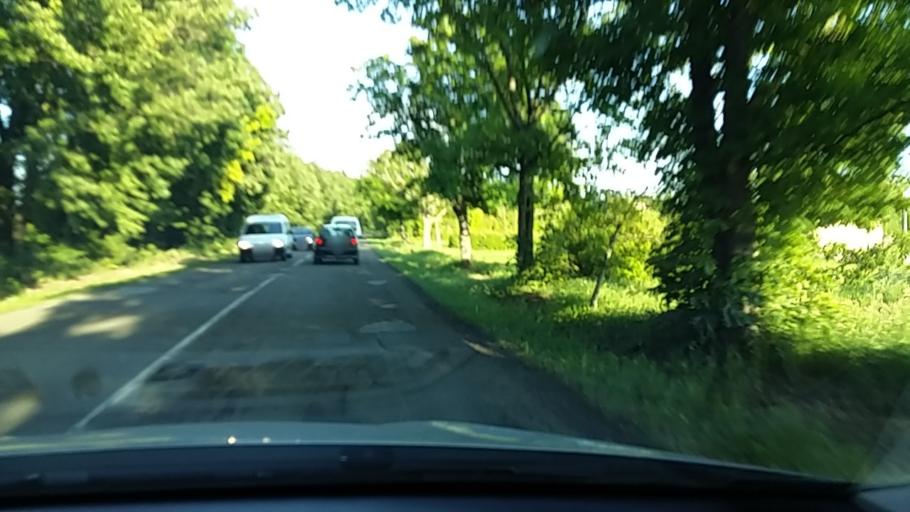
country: HU
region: Nograd
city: Retsag
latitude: 47.8894
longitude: 19.0963
